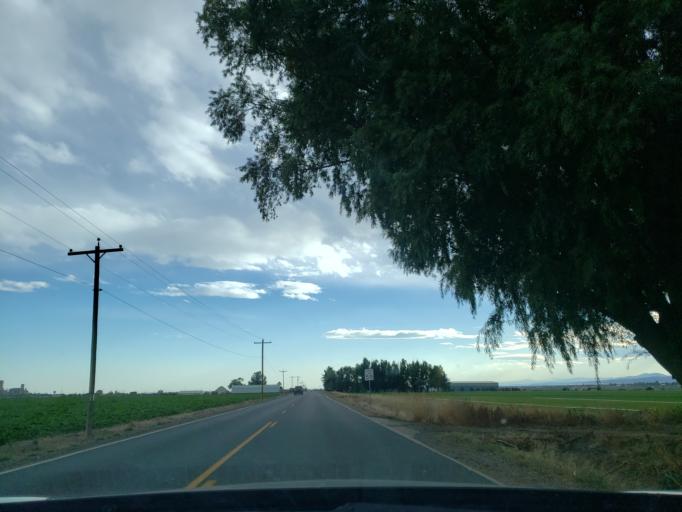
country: US
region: Colorado
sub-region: Larimer County
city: Wellington
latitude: 40.6379
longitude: -105.0197
